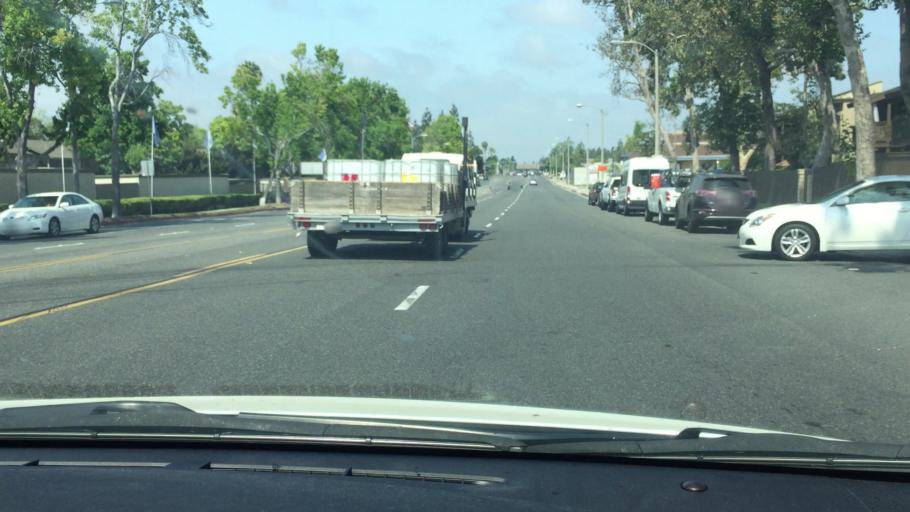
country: US
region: California
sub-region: Orange County
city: Costa Mesa
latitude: 33.6803
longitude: -117.8802
